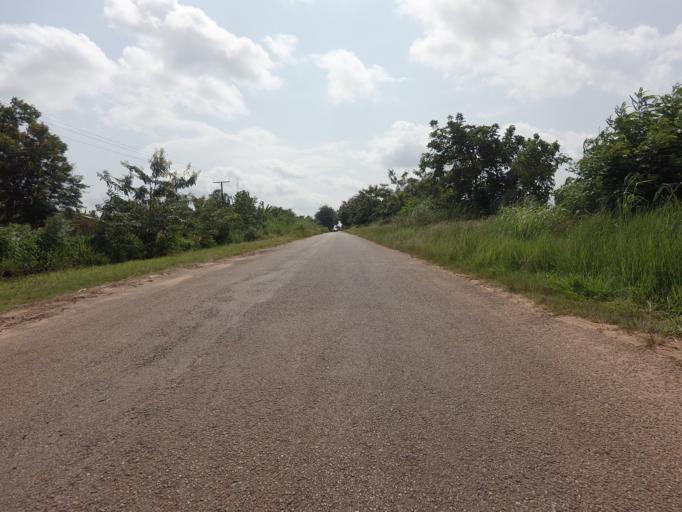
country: TG
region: Maritime
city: Lome
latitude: 6.2650
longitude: 0.9532
